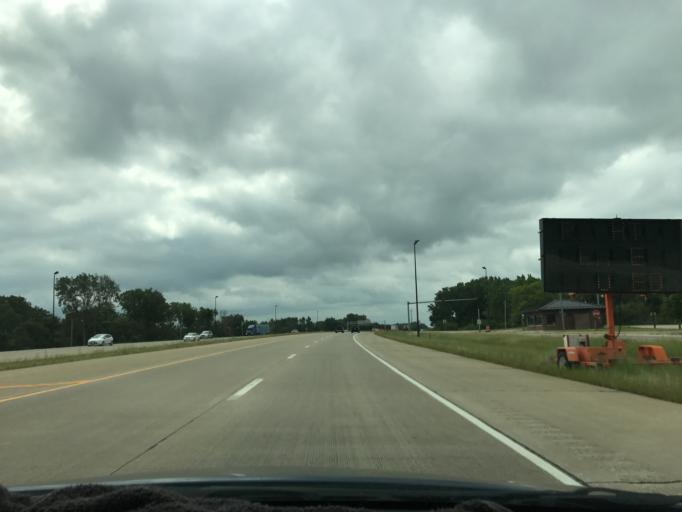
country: US
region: Iowa
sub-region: Scott County
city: Le Claire
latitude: 41.5574
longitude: -90.3425
